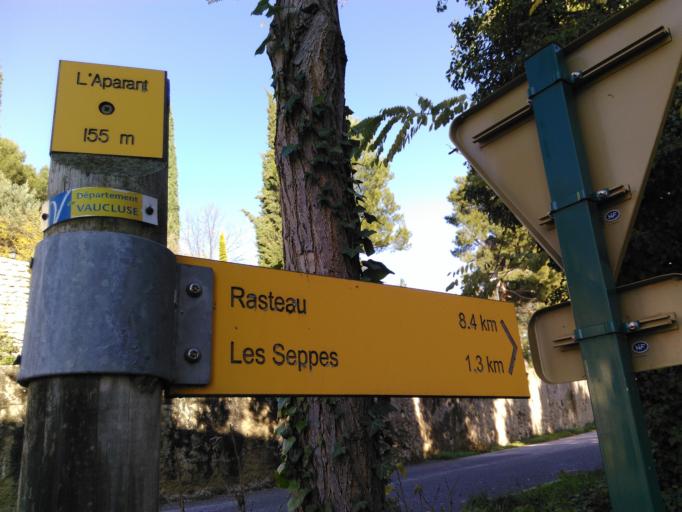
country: FR
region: Provence-Alpes-Cote d'Azur
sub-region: Departement du Vaucluse
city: Sainte-Cecile-les-Vignes
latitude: 44.2314
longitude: 4.9339
